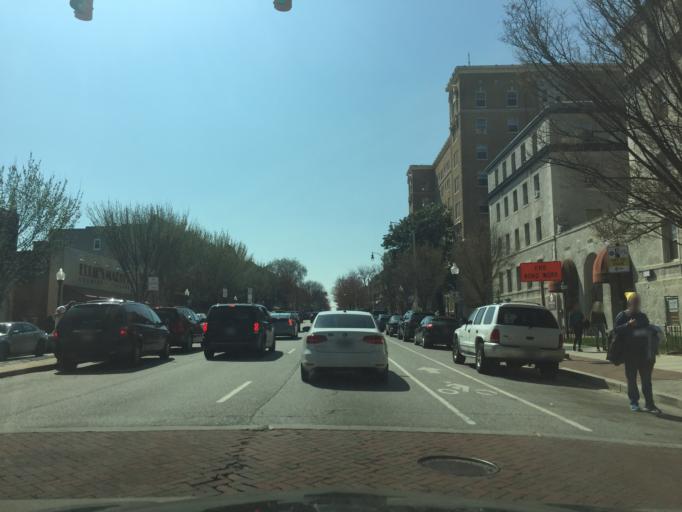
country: US
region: Maryland
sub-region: City of Baltimore
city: Baltimore
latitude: 39.3270
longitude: -76.6160
